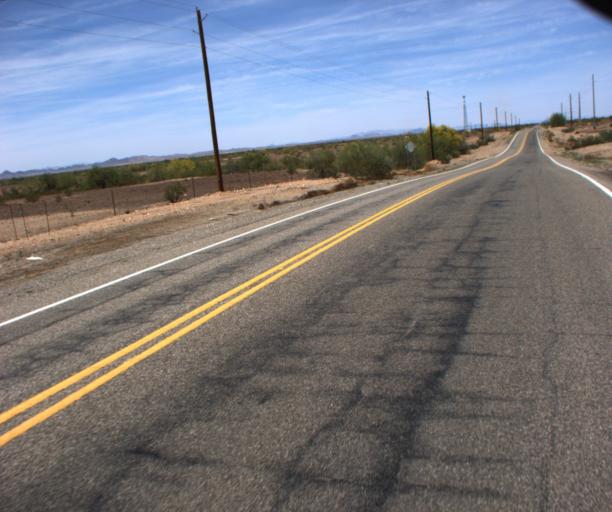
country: US
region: Arizona
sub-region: La Paz County
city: Quartzsite
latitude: 33.6915
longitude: -114.2170
